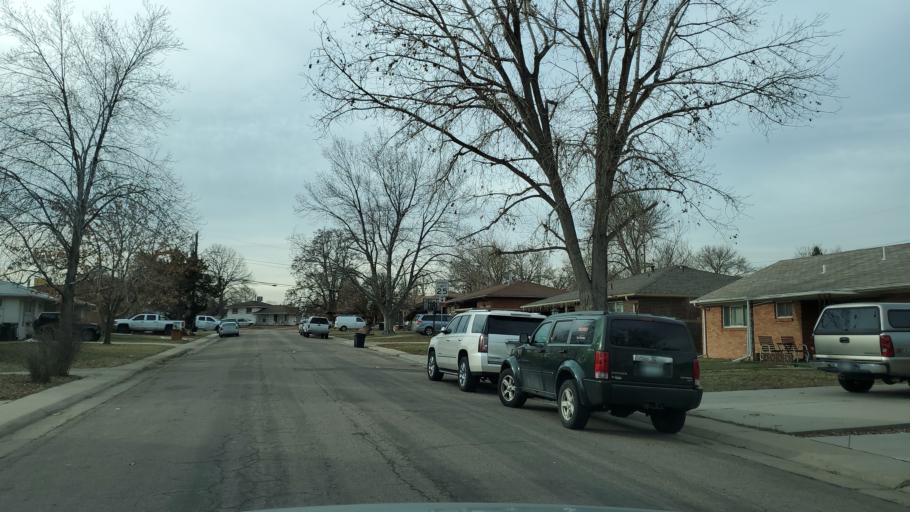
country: US
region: Colorado
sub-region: Adams County
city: Westminster
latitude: 39.8410
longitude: -105.0218
